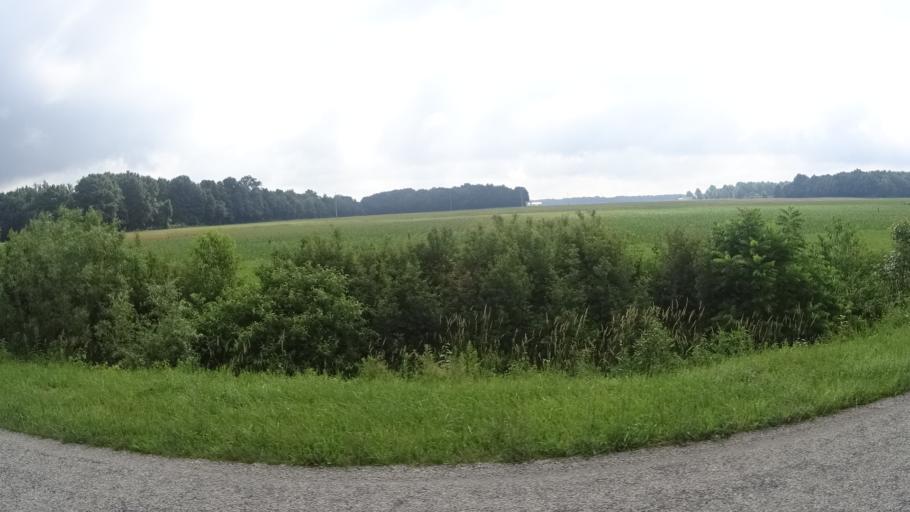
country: US
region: Ohio
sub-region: Huron County
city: Wakeman
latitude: 41.2950
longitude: -82.4810
